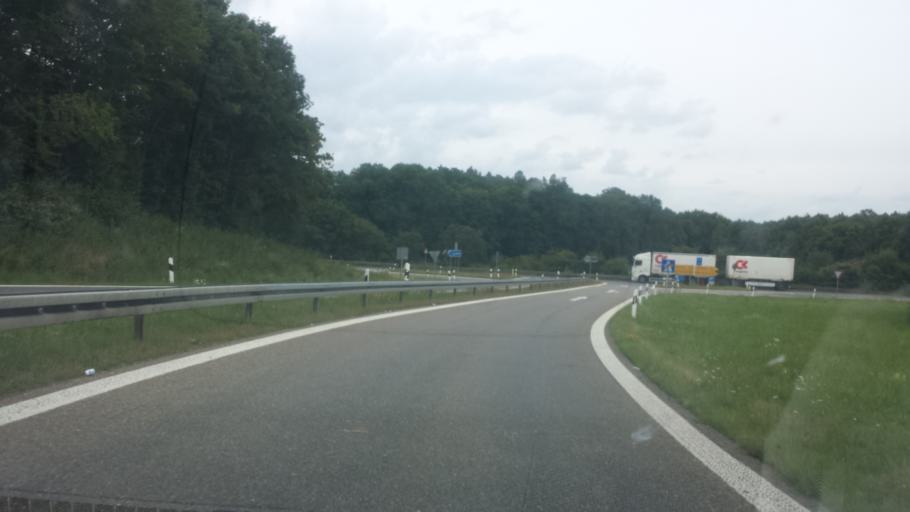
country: DE
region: Bavaria
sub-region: Regierungsbezirk Mittelfranken
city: Neuendettelsau
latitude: 49.3060
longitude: 10.7913
